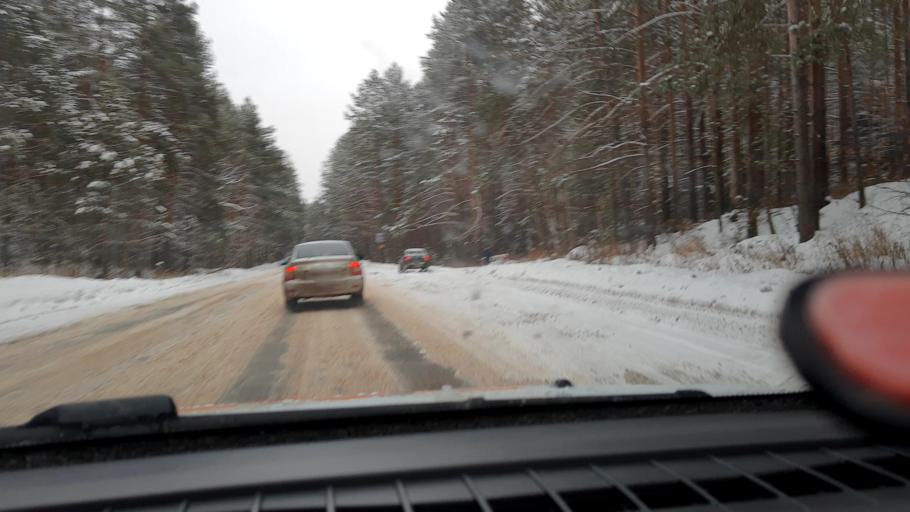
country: RU
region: Nizjnij Novgorod
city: Pamyat' Parizhskoy Kommuny
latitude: 56.2802
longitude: 44.3823
